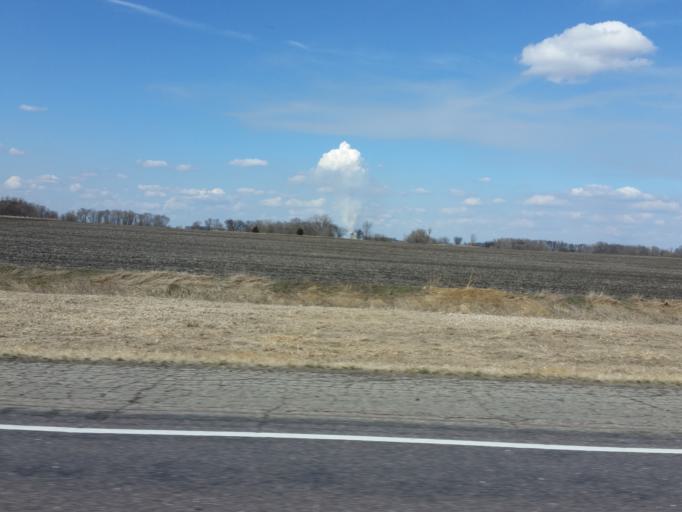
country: US
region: Minnesota
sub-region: Lac qui Parle County
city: Madison
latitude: 44.9359
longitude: -96.4222
